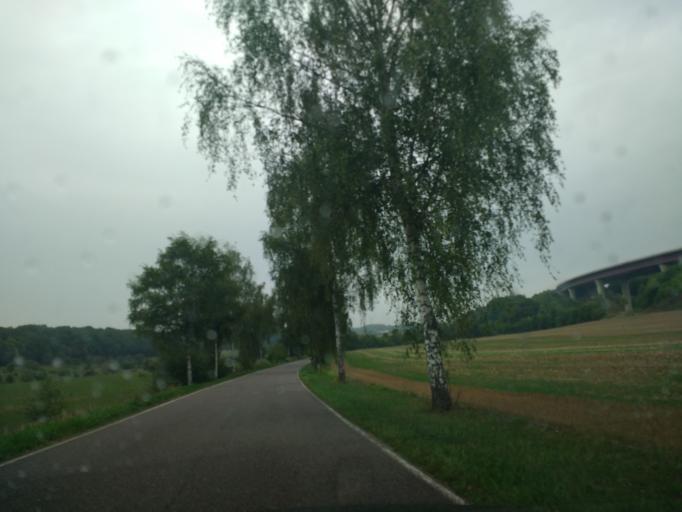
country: DE
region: Saarland
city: Perl
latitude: 49.4932
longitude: 6.3903
